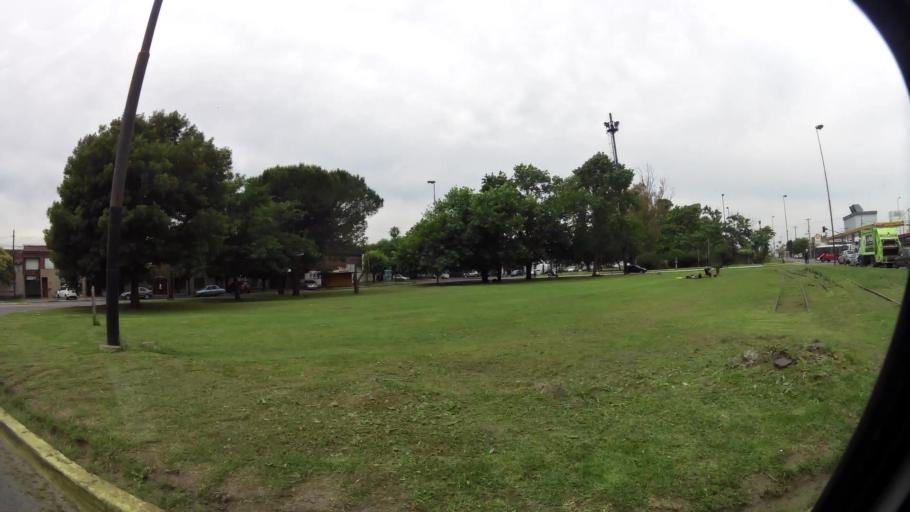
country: AR
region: Buenos Aires
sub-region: Partido de La Plata
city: La Plata
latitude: -34.9433
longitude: -57.9673
